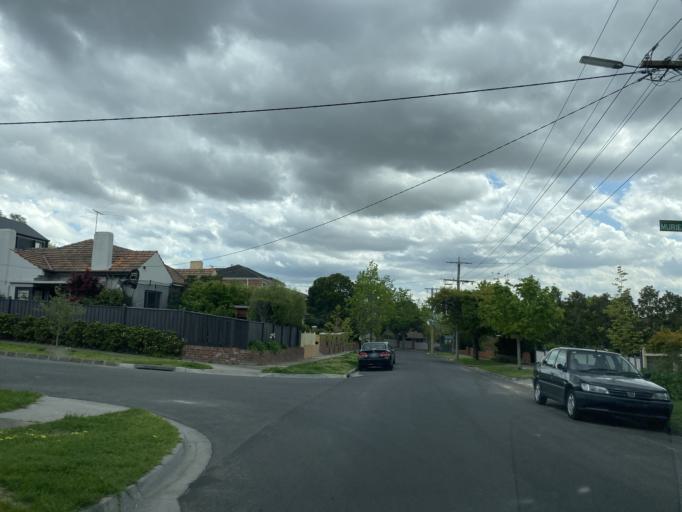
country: AU
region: Victoria
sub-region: Boroondara
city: Ashburton
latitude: -37.8525
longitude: 145.0880
